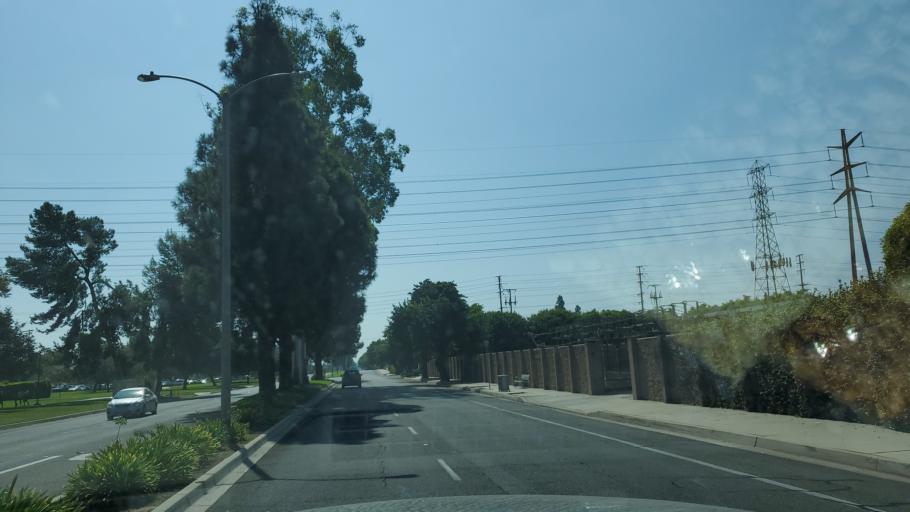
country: US
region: California
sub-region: Los Angeles County
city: Cerritos
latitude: 33.8513
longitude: -118.0635
